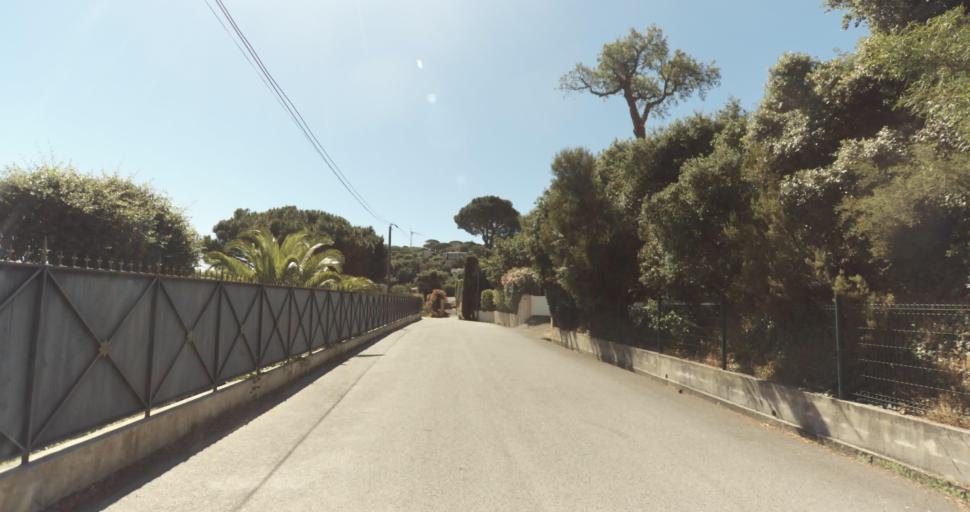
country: FR
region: Provence-Alpes-Cote d'Azur
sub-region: Departement du Var
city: Saint-Tropez
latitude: 43.2597
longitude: 6.6052
